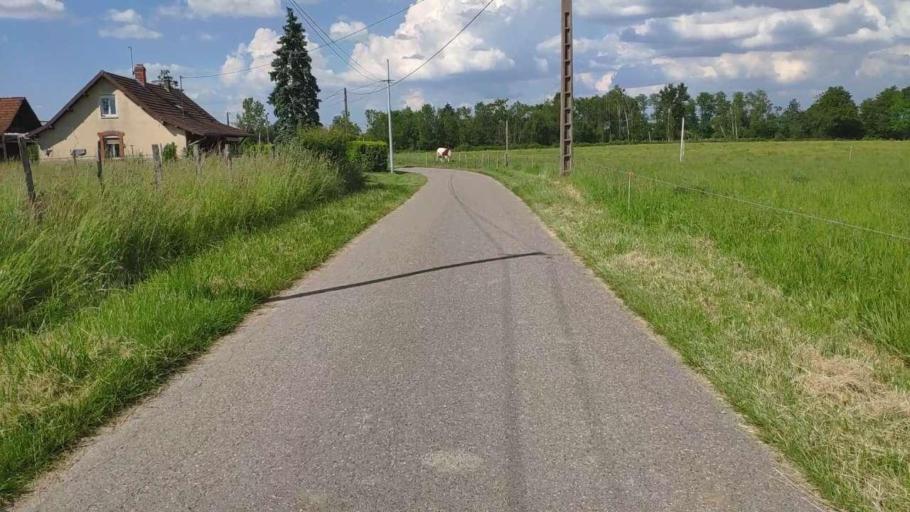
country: FR
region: Franche-Comte
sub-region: Departement du Jura
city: Bletterans
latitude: 46.8145
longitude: 5.3928
